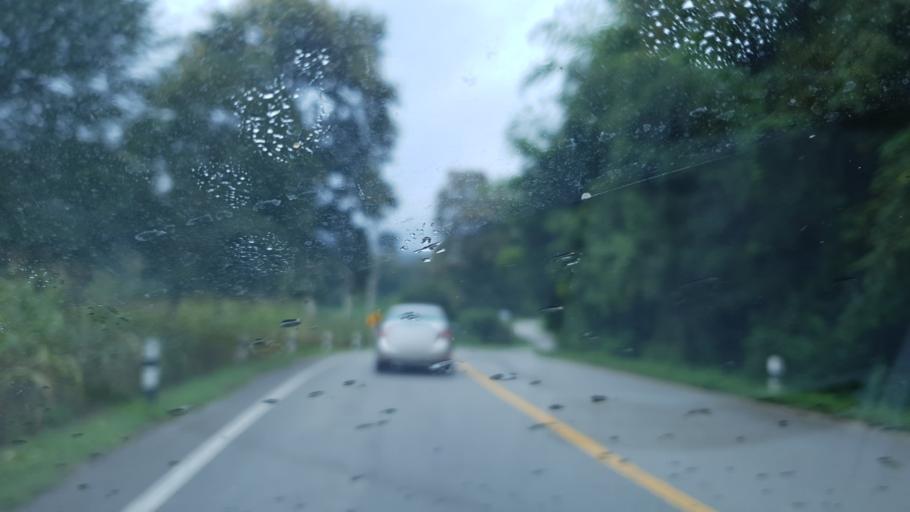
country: TH
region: Mae Hong Son
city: Khun Yuam
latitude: 18.7067
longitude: 97.9125
